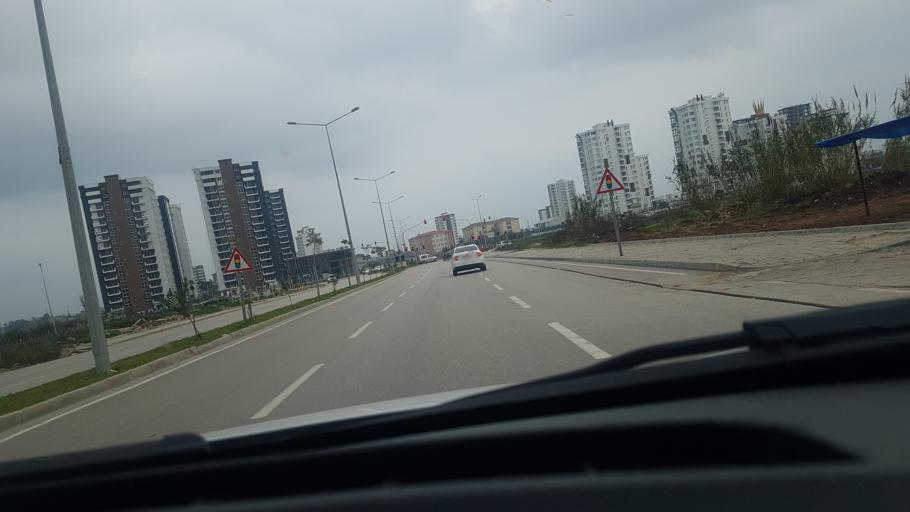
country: TR
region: Adana
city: Seyhan
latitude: 37.0168
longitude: 35.2578
